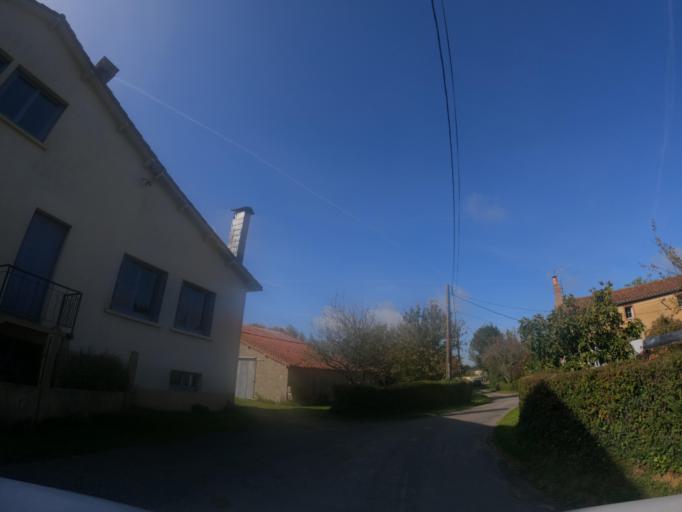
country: FR
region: Poitou-Charentes
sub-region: Departement des Deux-Sevres
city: Courlay
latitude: 46.7932
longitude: -0.5608
